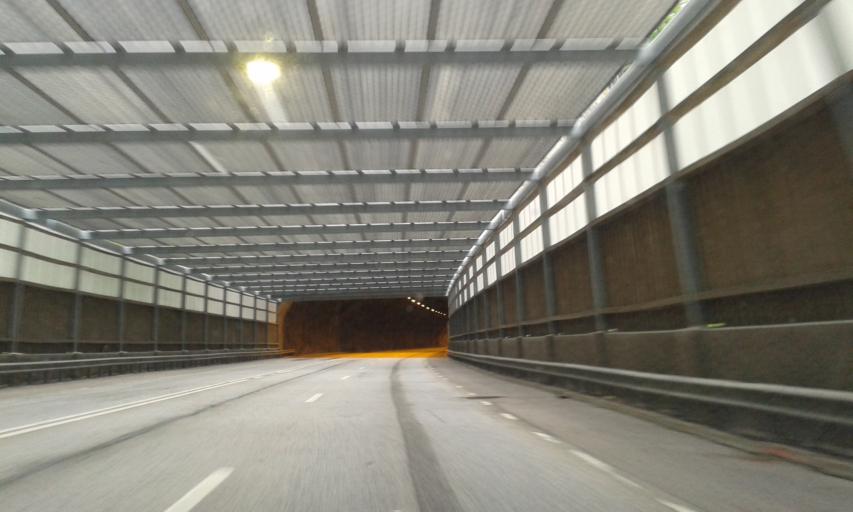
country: SE
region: Vaestra Goetaland
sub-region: Goteborg
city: Gardsten
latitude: 57.7995
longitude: 12.0216
